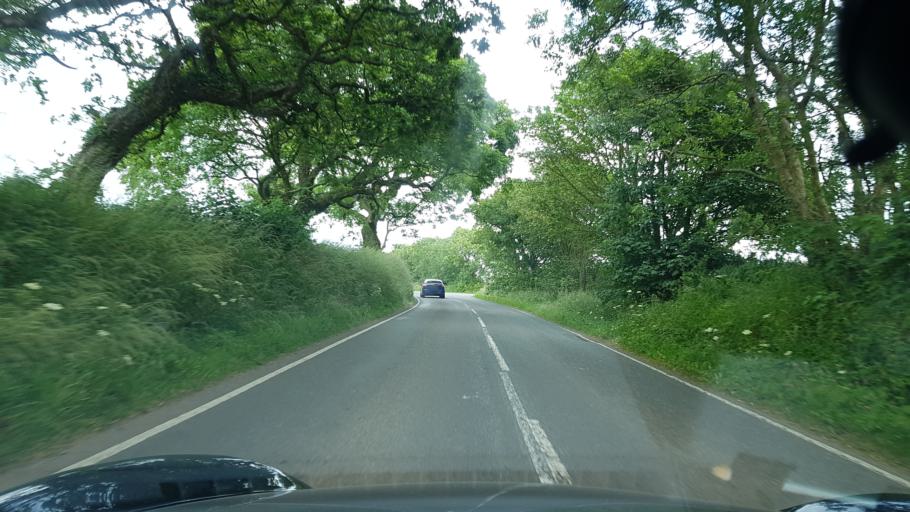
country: GB
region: Wales
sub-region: Pembrokeshire
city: Herbrandston
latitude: 51.7681
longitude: -5.0685
